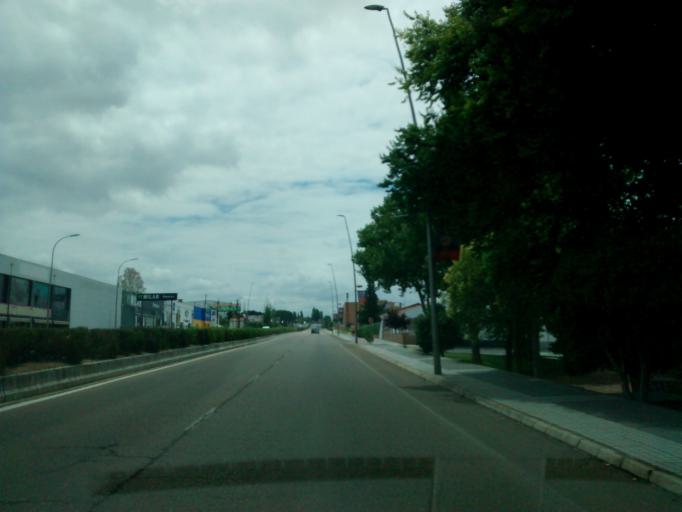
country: ES
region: Extremadura
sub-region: Provincia de Badajoz
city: Merida
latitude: 38.9213
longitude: -6.3285
